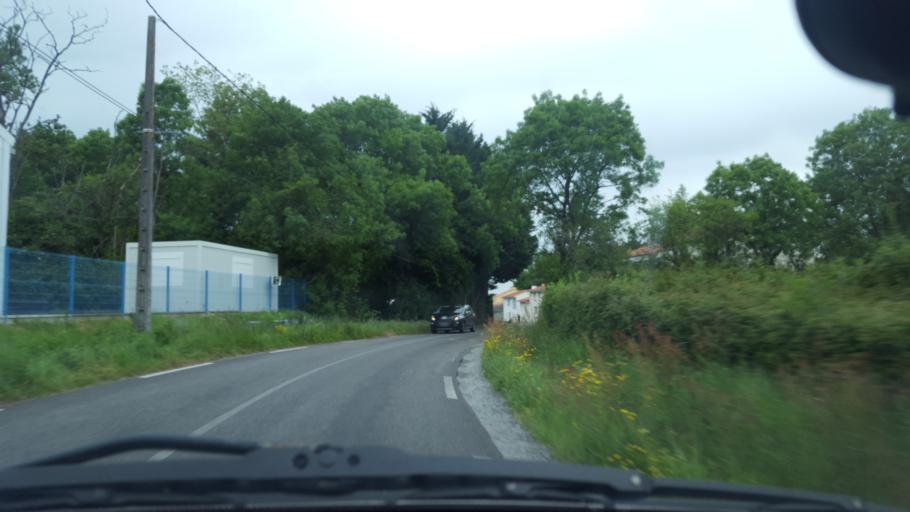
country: FR
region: Pays de la Loire
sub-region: Departement de la Loire-Atlantique
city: Les Sorinieres
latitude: 47.1543
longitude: -1.5049
